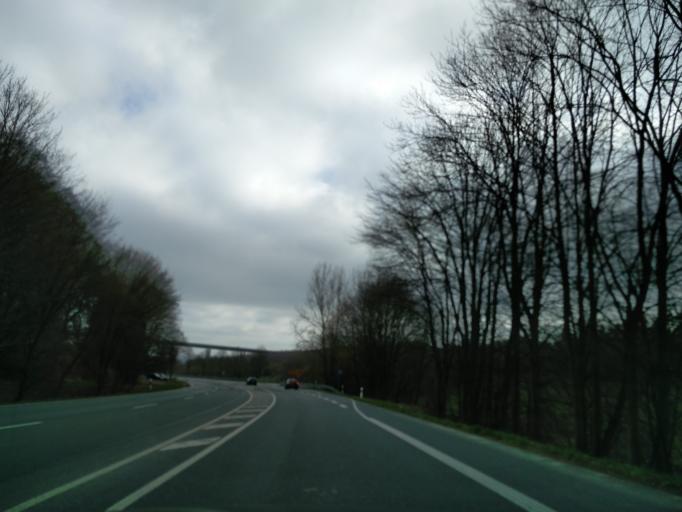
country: DE
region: North Rhine-Westphalia
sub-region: Regierungsbezirk Detmold
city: Willebadessen
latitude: 51.5401
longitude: 9.0132
